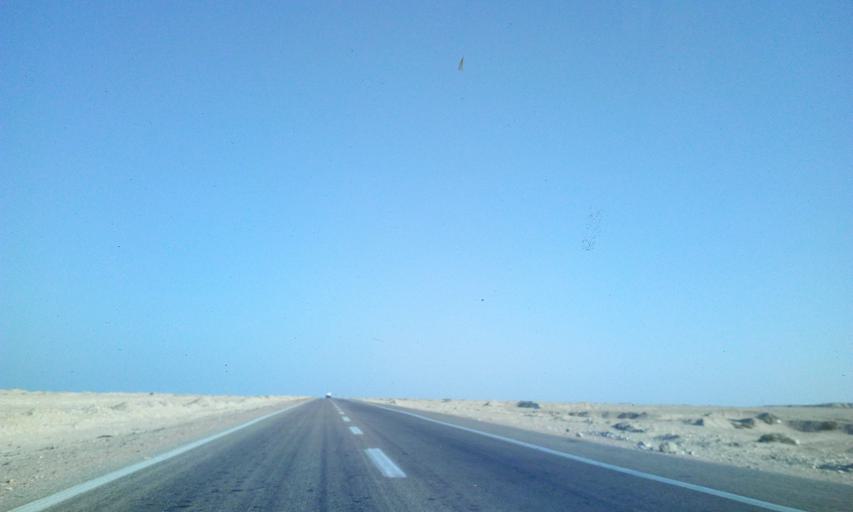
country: EG
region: As Suways
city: Ain Sukhna
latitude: 28.8385
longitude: 32.7063
